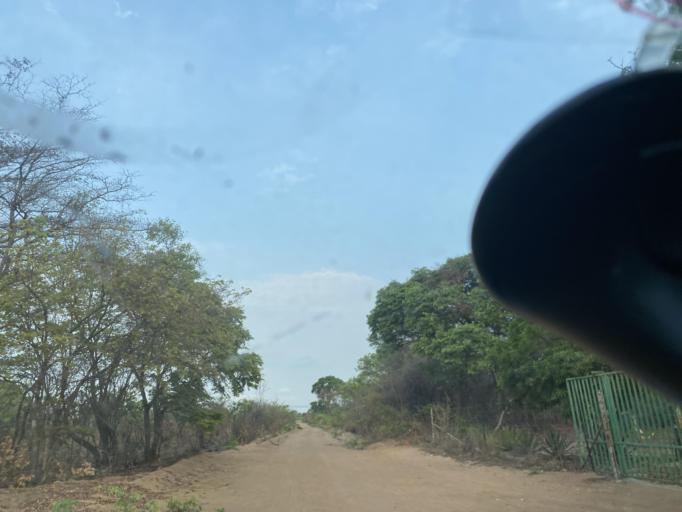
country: ZM
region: Lusaka
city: Chongwe
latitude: -15.2043
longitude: 28.5147
